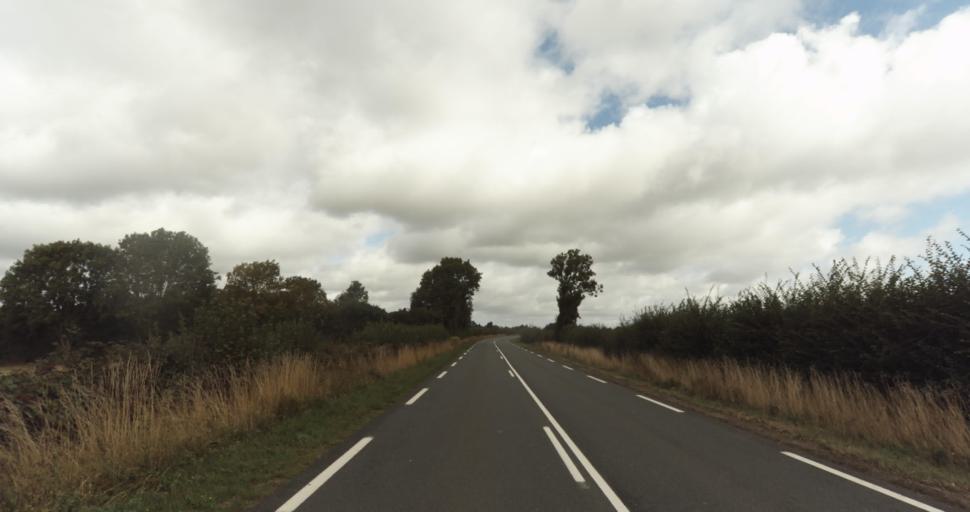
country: FR
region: Lower Normandy
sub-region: Departement de l'Orne
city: Vimoutiers
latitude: 48.8664
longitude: 0.2527
